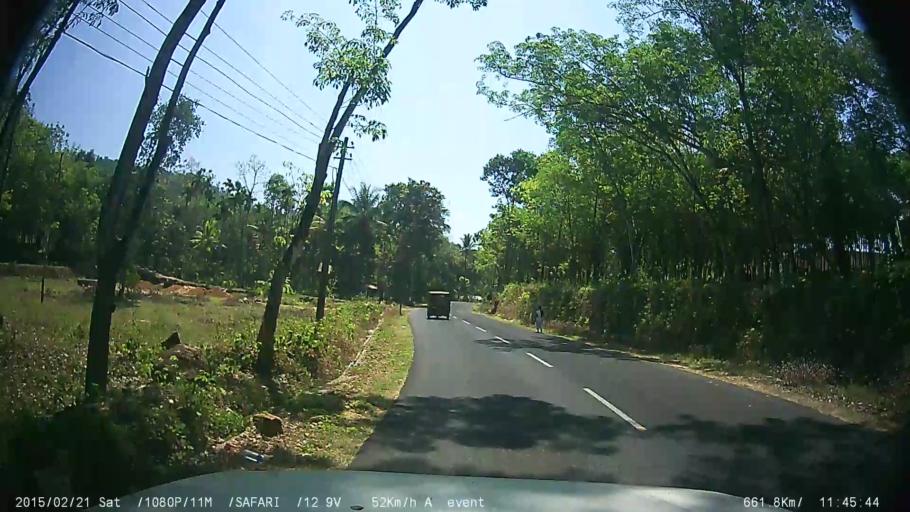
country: IN
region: Kerala
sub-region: Kottayam
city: Lalam
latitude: 9.7787
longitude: 76.7231
